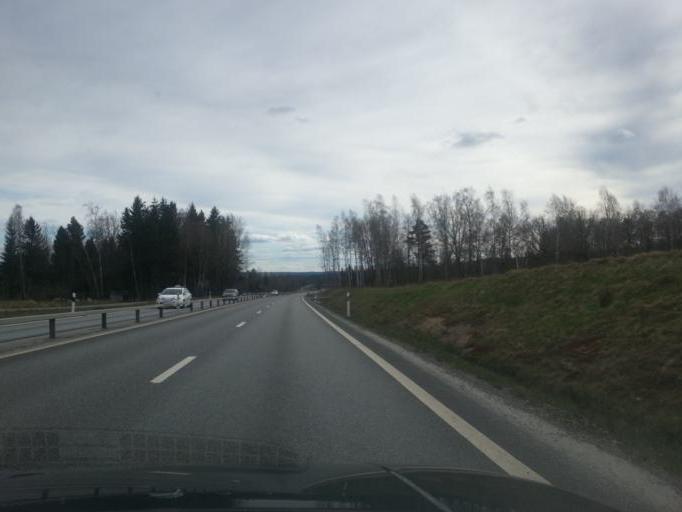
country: SE
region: Joenkoeping
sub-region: Habo Kommun
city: Habo
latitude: 57.8966
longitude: 14.1054
